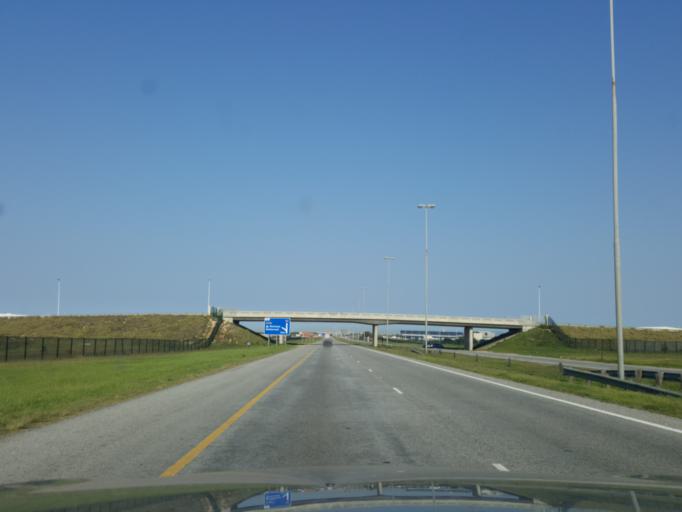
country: ZA
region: Eastern Cape
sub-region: Nelson Mandela Bay Metropolitan Municipality
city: Port Elizabeth
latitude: -33.8110
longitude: 25.6520
